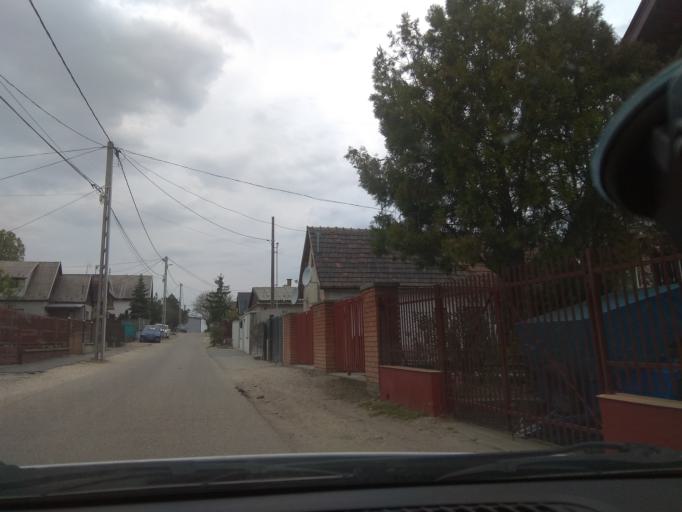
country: HU
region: Pest
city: Halasztelek
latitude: 47.3777
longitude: 19.0115
